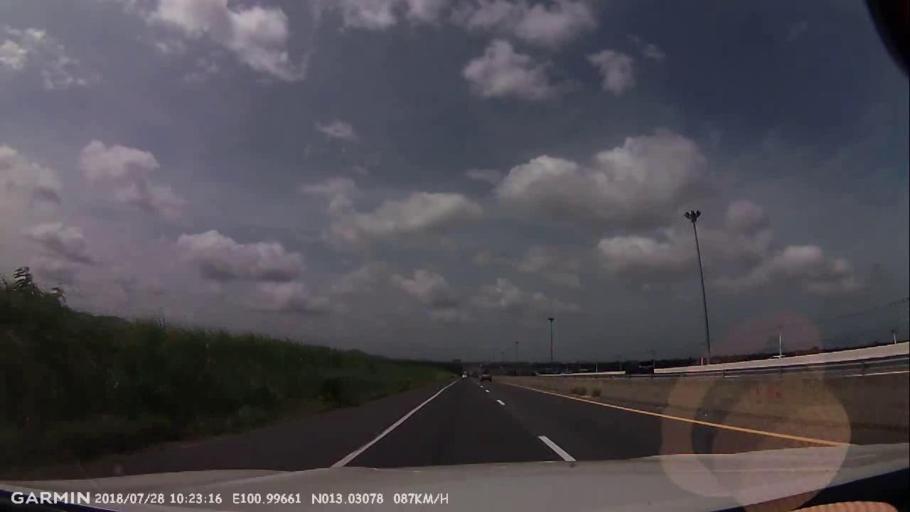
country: TH
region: Chon Buri
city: Ban Talat Bueng
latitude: 13.0303
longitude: 100.9966
